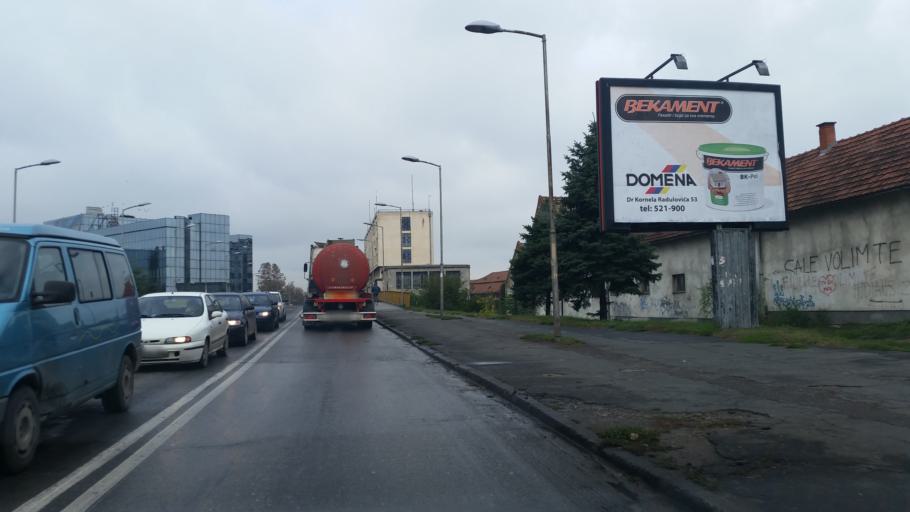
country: RS
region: Autonomna Pokrajina Vojvodina
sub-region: Srednjebanatski Okrug
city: Zrenjanin
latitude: 45.3790
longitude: 20.3993
